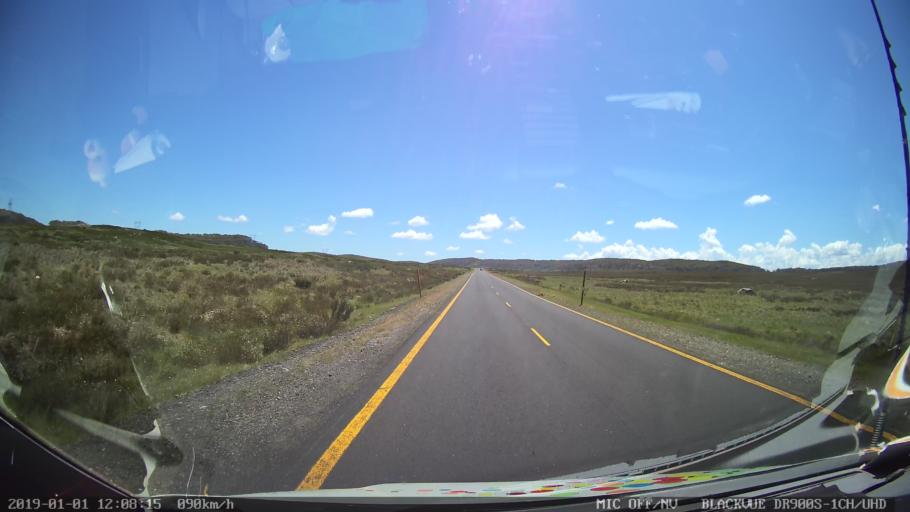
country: AU
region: New South Wales
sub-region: Tumut Shire
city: Tumut
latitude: -35.8227
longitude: 148.4938
